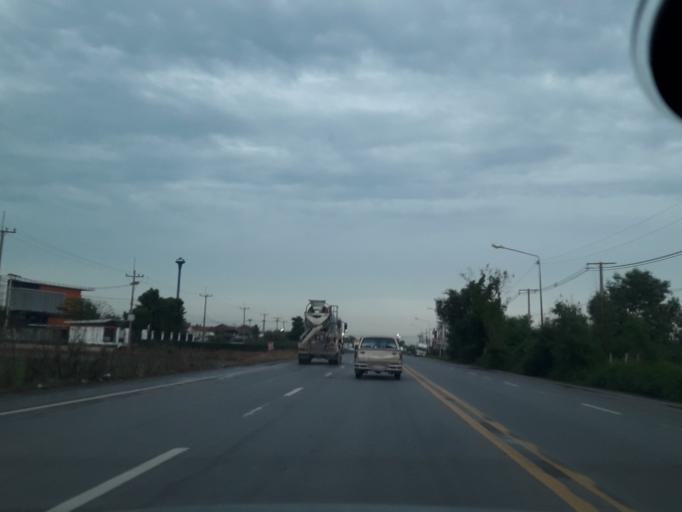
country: TH
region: Pathum Thani
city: Ban Rangsit
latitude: 14.0504
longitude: 100.7478
